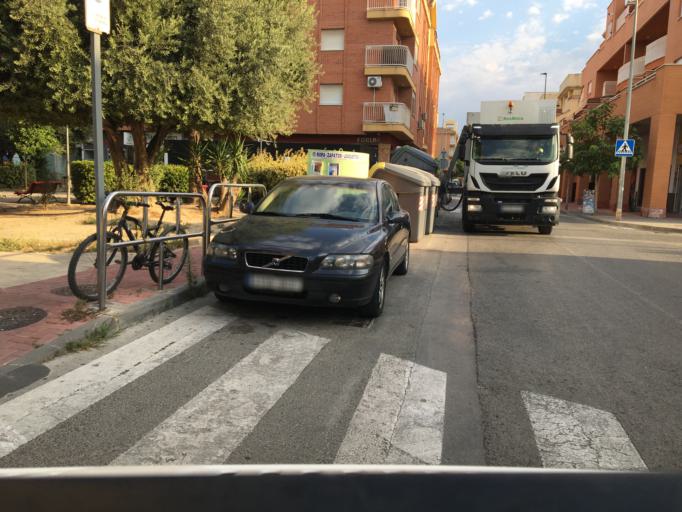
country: ES
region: Murcia
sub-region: Murcia
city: Alcantarilla
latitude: 37.9701
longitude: -1.2067
